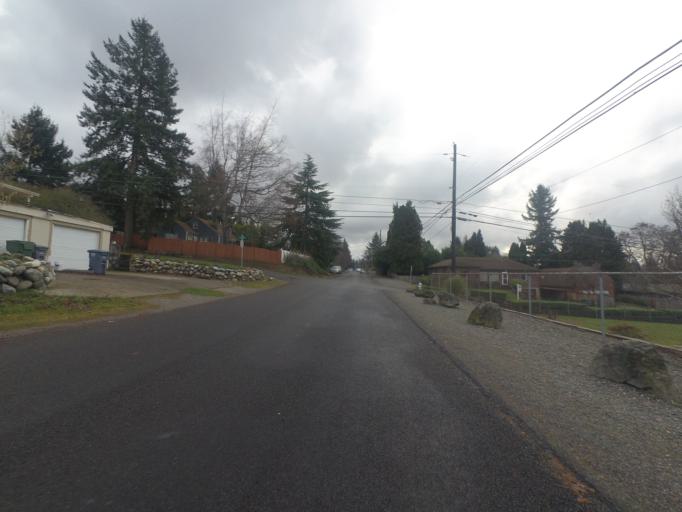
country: US
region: Washington
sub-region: Pierce County
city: University Place
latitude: 47.2338
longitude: -122.5391
